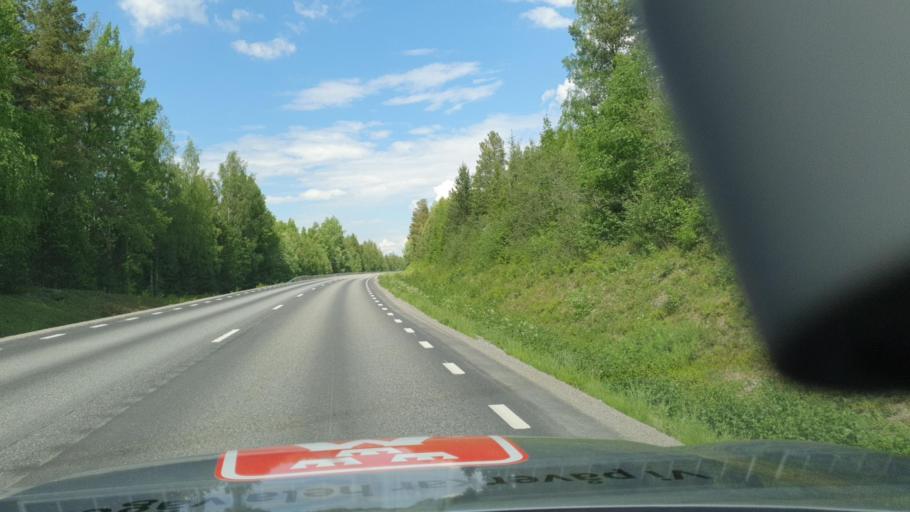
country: SE
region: Vaesternorrland
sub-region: Solleftea Kommun
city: As
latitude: 63.5211
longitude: 16.8340
